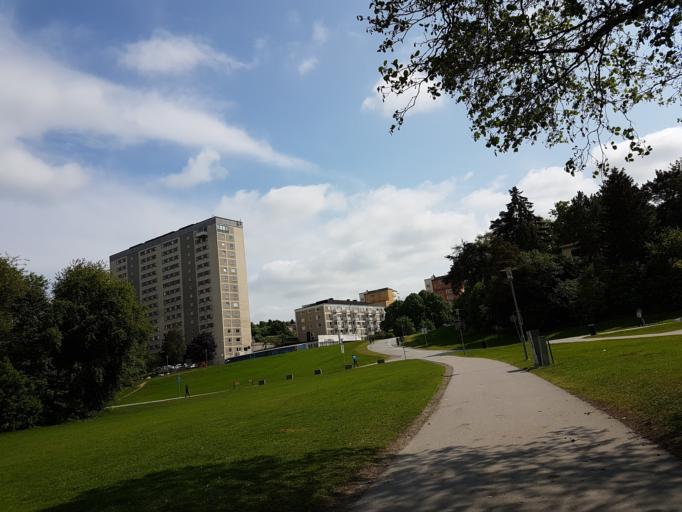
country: SE
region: Stockholm
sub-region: Sundbybergs Kommun
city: Sundbyberg
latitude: 59.3711
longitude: 17.9726
